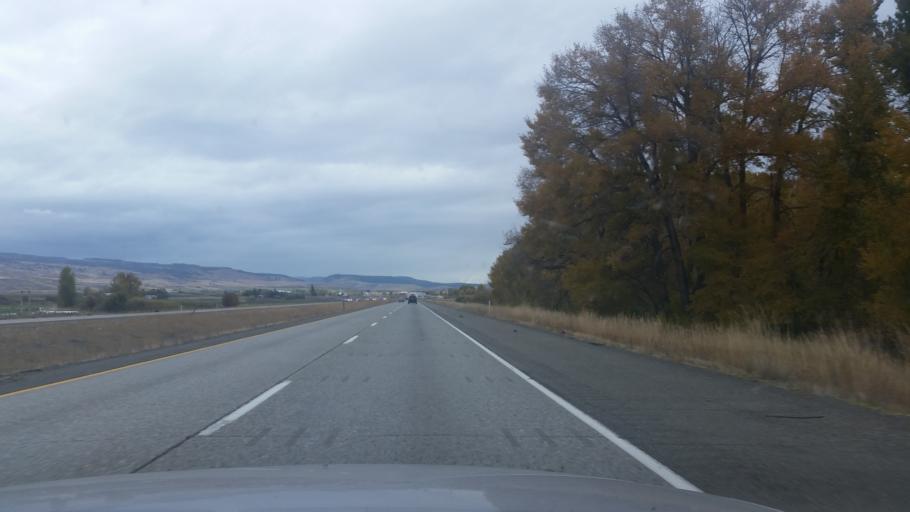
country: US
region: Washington
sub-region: Kittitas County
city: Ellensburg
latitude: 47.0466
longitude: -120.6450
